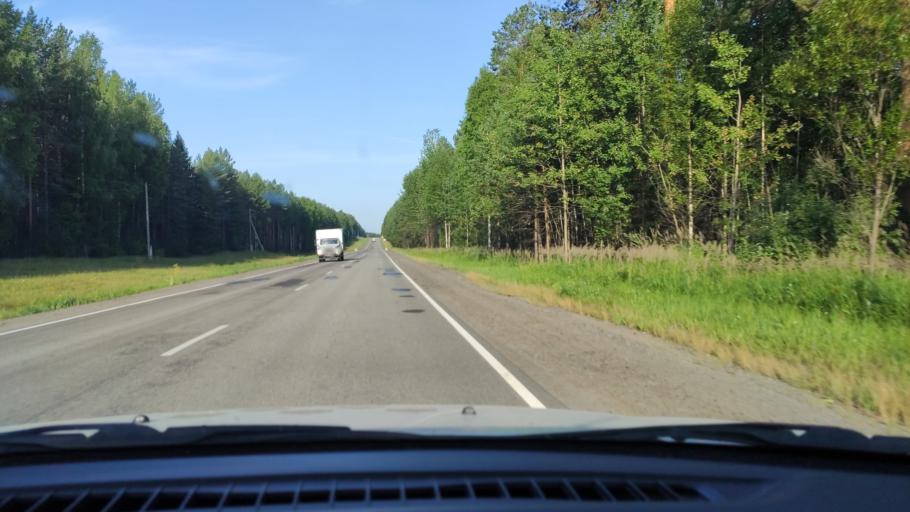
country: RU
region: Kirov
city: Belaya Kholunitsa
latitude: 58.9070
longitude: 50.9724
